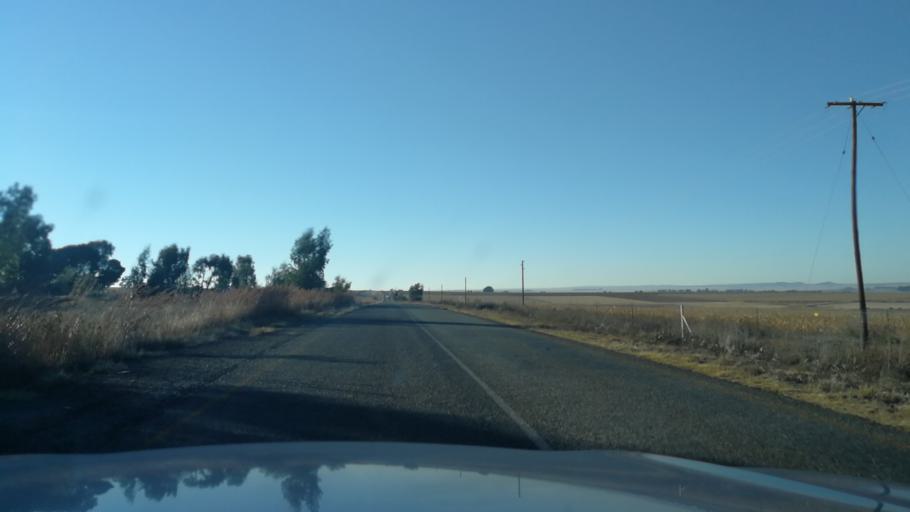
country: ZA
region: North-West
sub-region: Bojanala Platinum District Municipality
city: Koster
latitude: -25.9132
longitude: 27.0571
